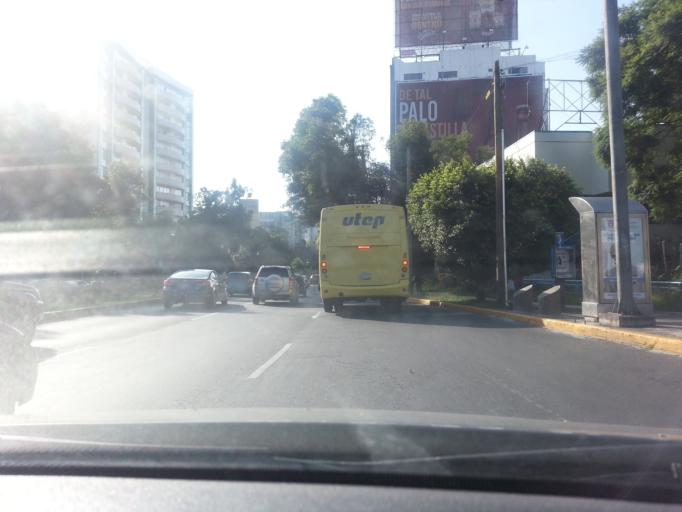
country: MX
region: Mexico City
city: Alvaro Obregon
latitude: 19.3675
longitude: -99.1807
